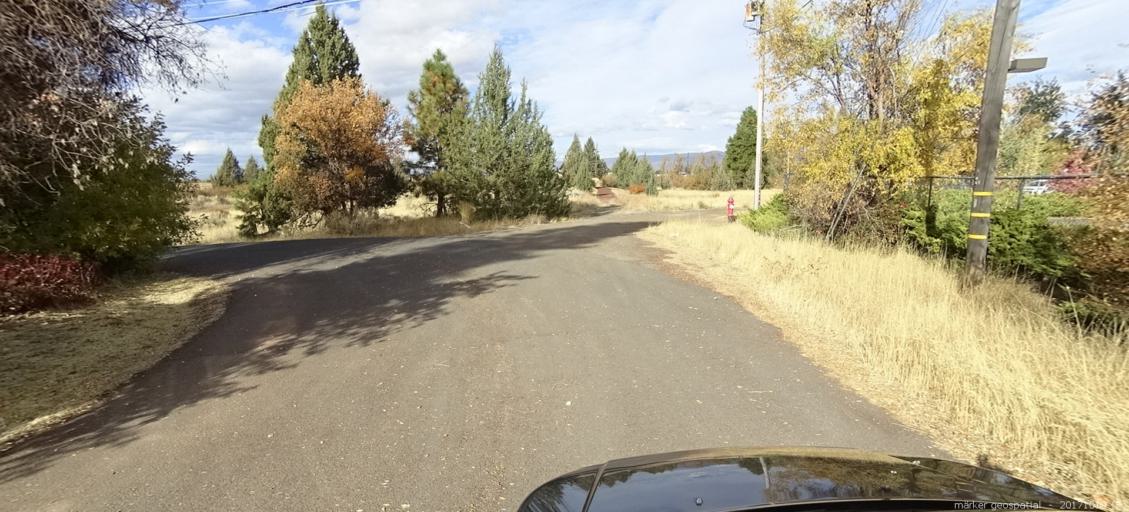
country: US
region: California
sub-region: Shasta County
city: Burney
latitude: 41.0122
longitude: -121.4354
